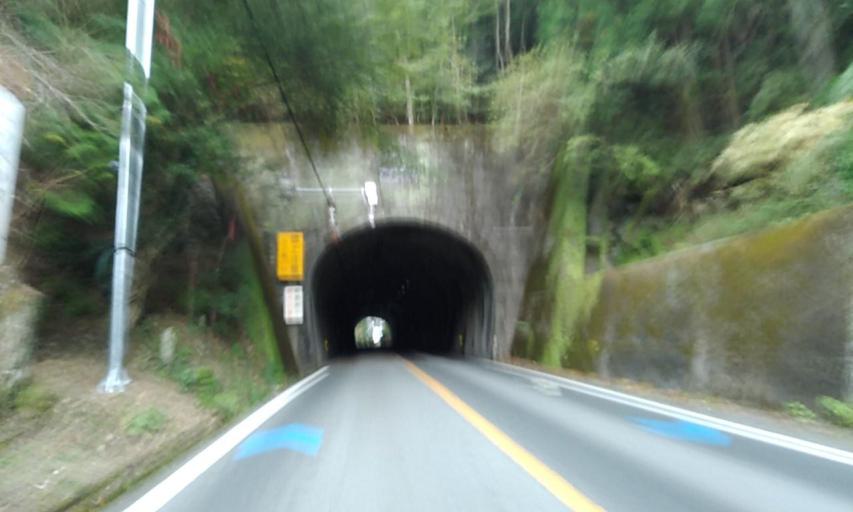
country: JP
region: Mie
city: Ise
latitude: 34.2927
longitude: 136.5309
